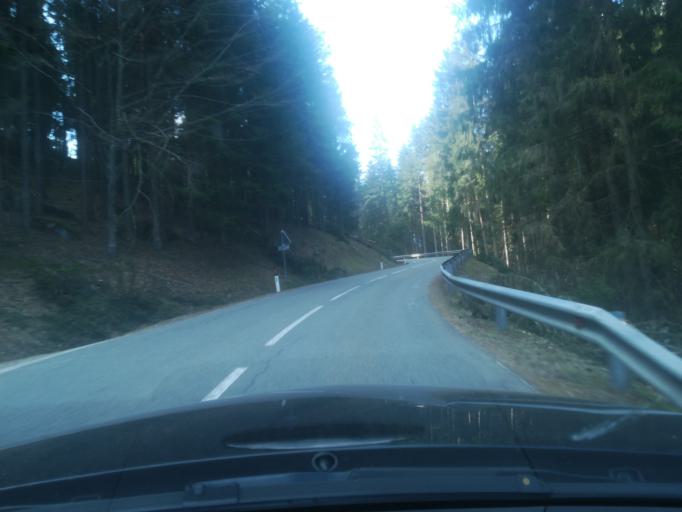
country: AT
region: Lower Austria
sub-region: Politischer Bezirk Zwettl
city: Langschlag
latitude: 48.4590
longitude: 14.7102
